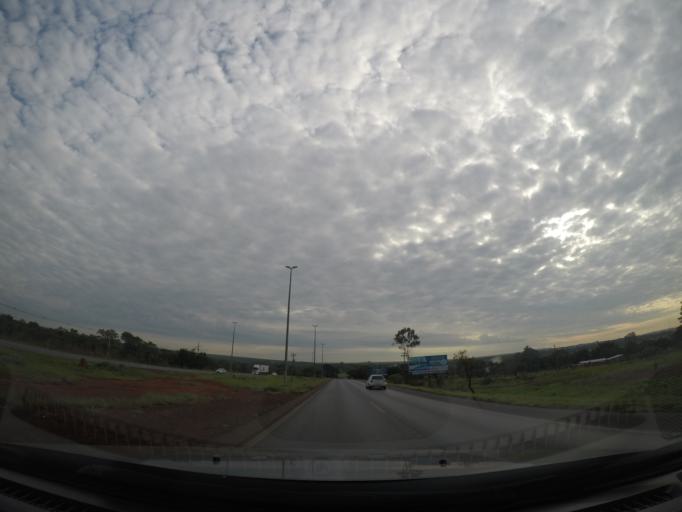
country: BR
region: Goias
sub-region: Planaltina
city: Planaltina
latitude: -15.5970
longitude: -47.6729
